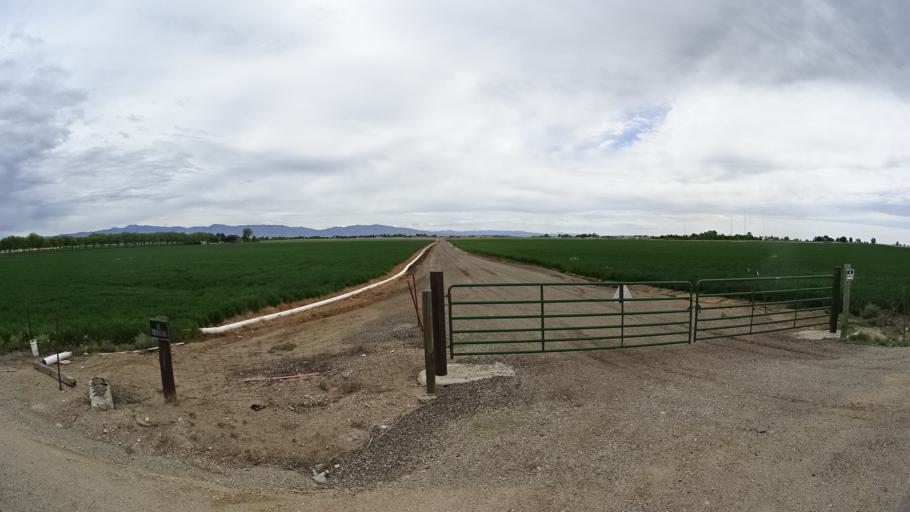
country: US
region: Idaho
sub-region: Ada County
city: Meridian
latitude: 43.5682
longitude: -116.4138
